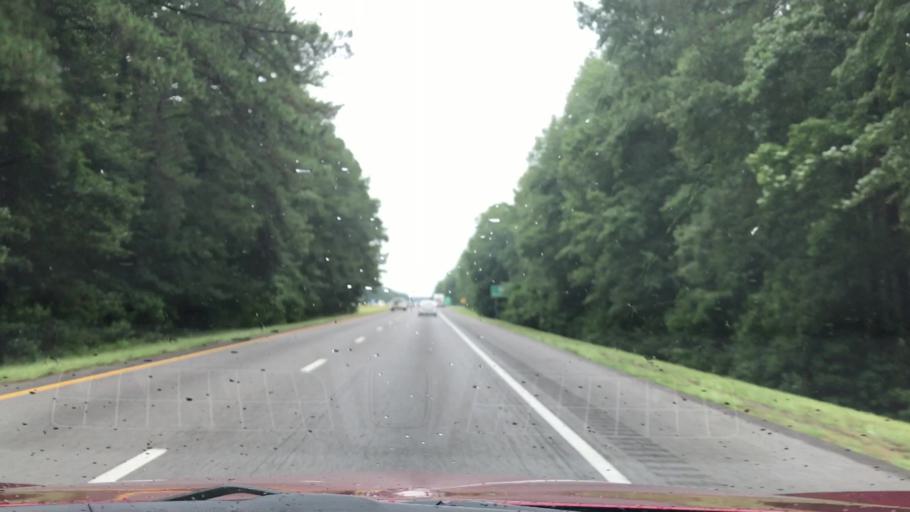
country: US
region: South Carolina
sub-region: Dorchester County
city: Ridgeville
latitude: 33.1398
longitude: -80.3164
